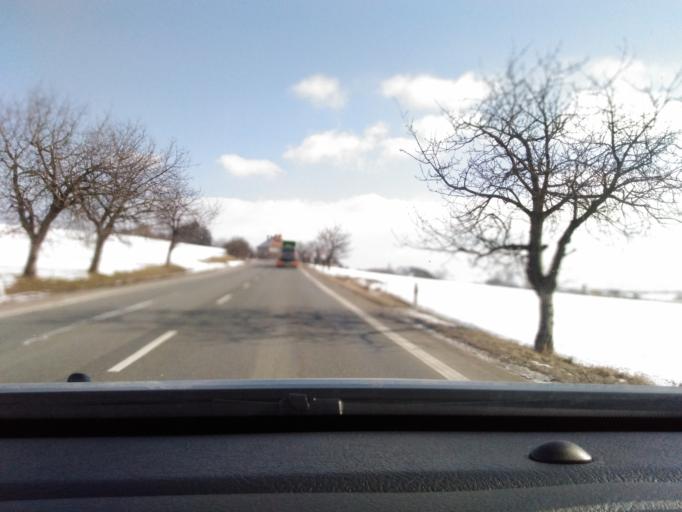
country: CZ
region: Vysocina
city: Krizanov
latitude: 49.3170
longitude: 16.1339
